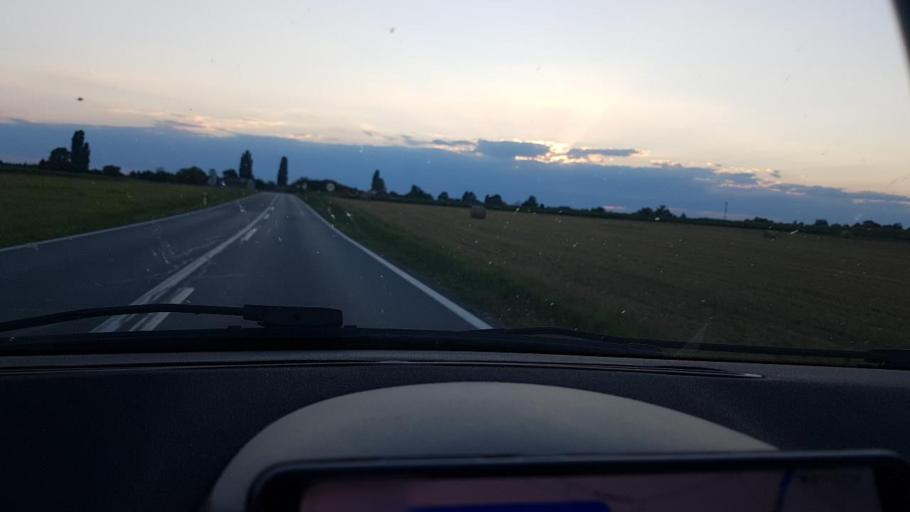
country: HR
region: Bjelovarsko-Bilogorska
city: Zdralovi
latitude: 45.8517
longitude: 16.9380
